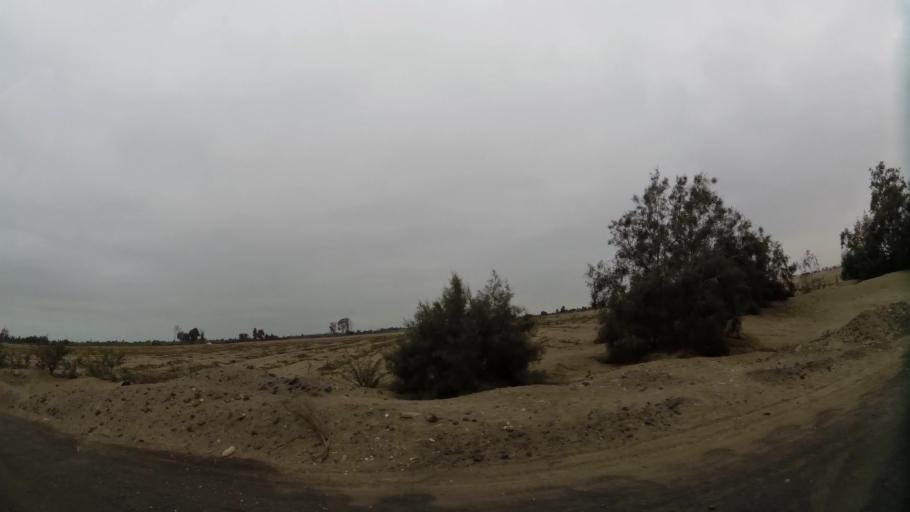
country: PE
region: Ica
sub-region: Provincia de Pisco
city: Pisco
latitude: -13.7553
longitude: -76.1823
